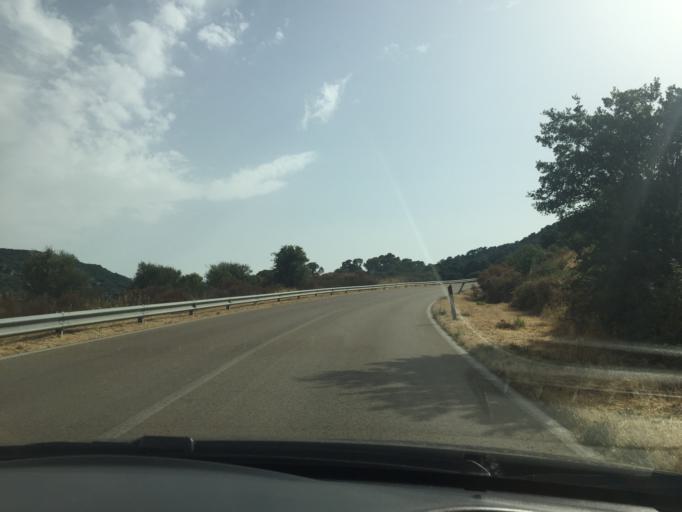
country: IT
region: Sardinia
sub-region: Provincia di Olbia-Tempio
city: Luras
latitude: 40.9546
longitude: 9.2065
